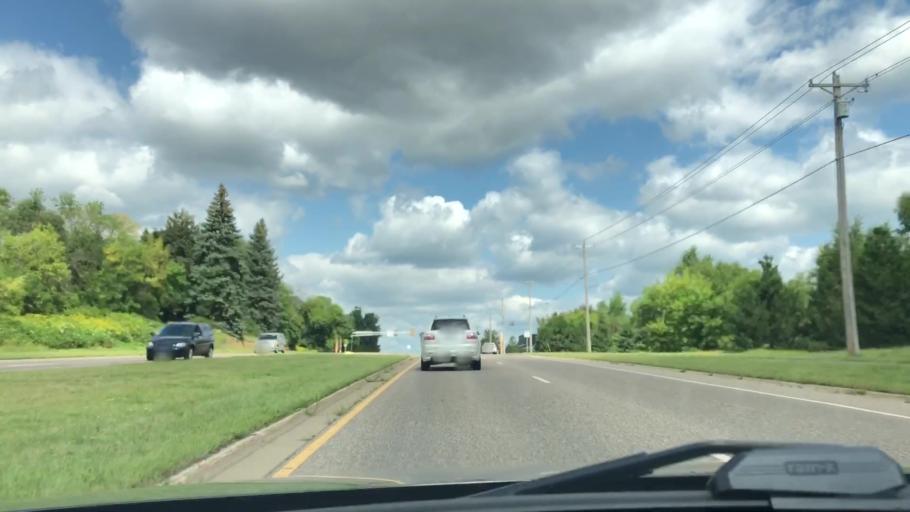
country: US
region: Minnesota
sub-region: Dakota County
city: Eagan
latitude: 44.8354
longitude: -93.1468
